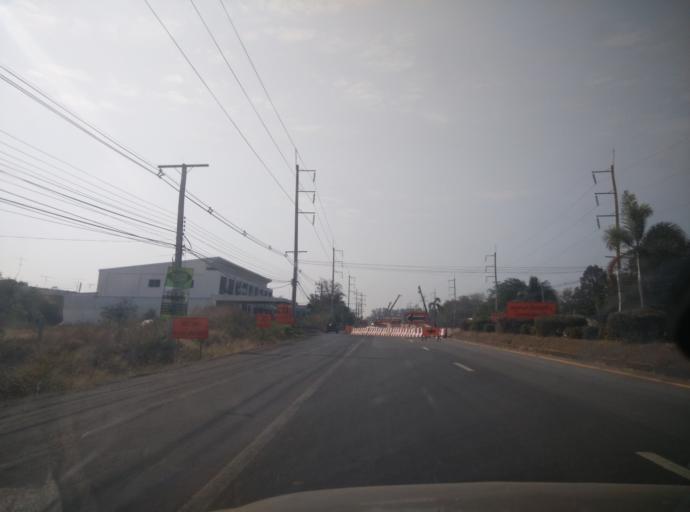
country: TH
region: Sisaket
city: Si Sa Ket
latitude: 15.1246
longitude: 104.2847
